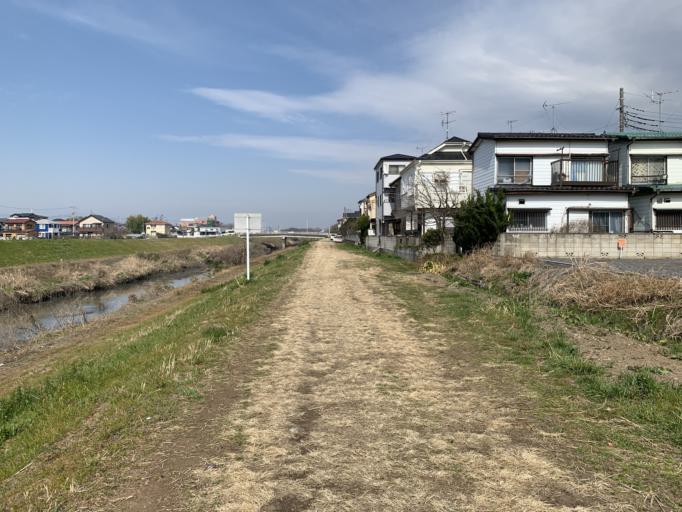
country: JP
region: Saitama
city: Yono
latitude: 35.8803
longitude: 139.6021
